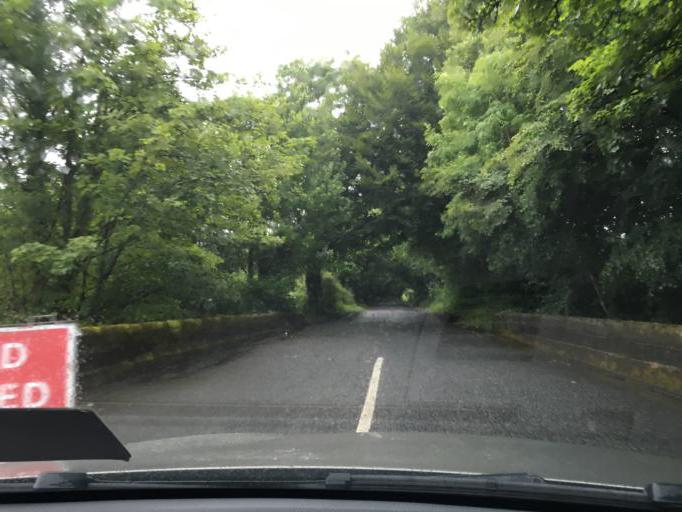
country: GB
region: Northern Ireland
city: Irvinestown
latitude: 54.5520
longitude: -7.8333
